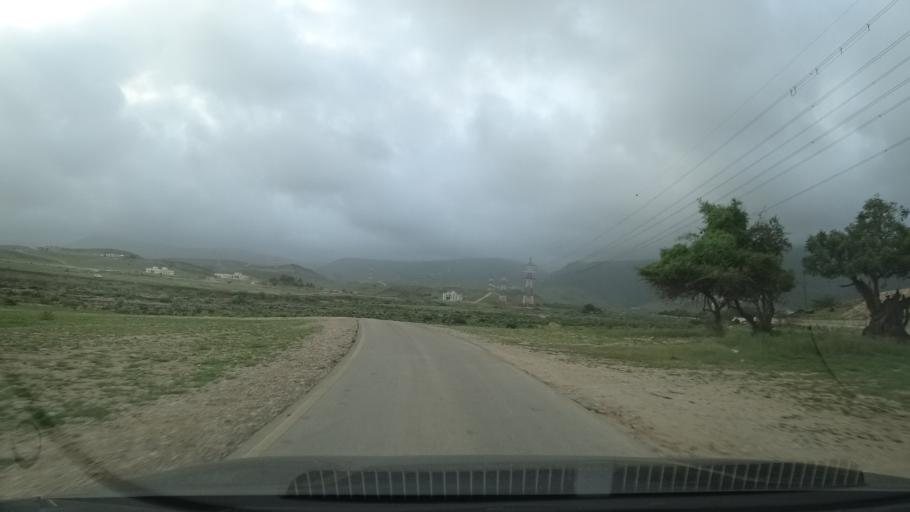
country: OM
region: Zufar
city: Salalah
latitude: 17.1154
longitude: 54.2269
